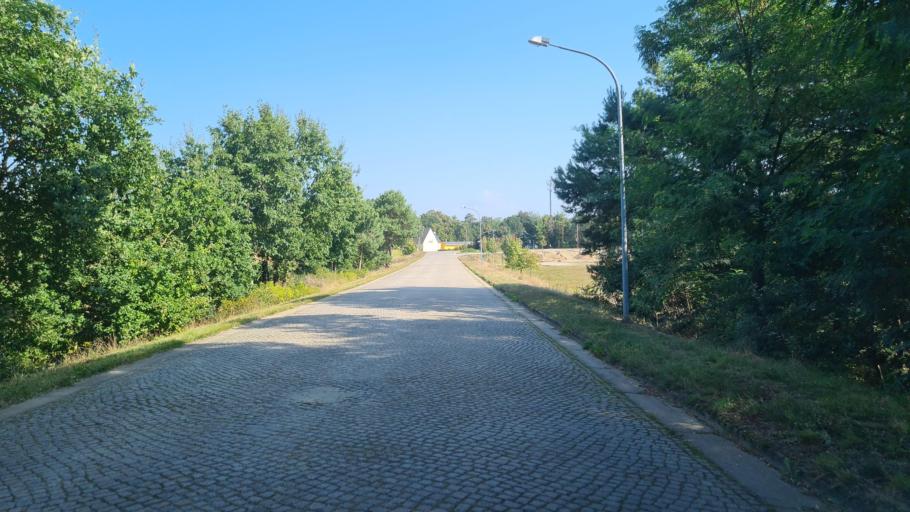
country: DE
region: Brandenburg
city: Kolkwitz
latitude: 51.7202
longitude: 14.2752
